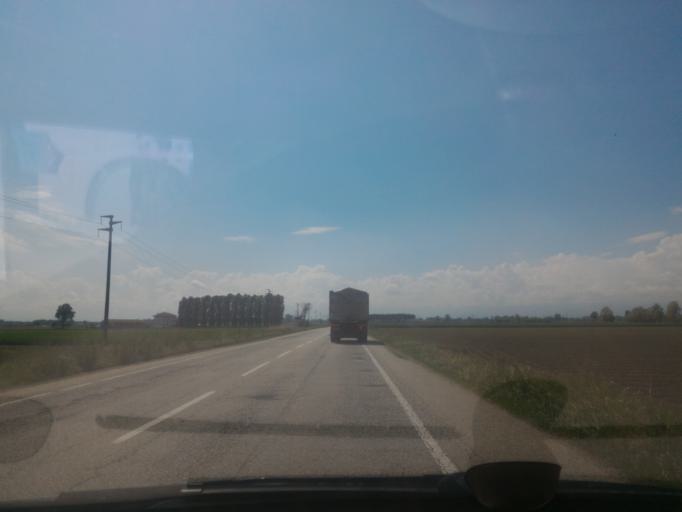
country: IT
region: Piedmont
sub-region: Provincia di Torino
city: Villastellone
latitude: 44.9203
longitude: 7.7245
